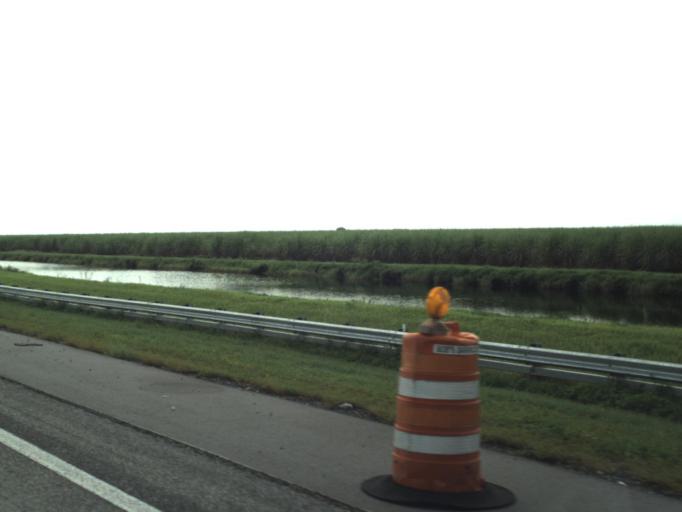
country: US
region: Florida
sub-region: Palm Beach County
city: Belle Glade
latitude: 26.7258
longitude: -80.5500
